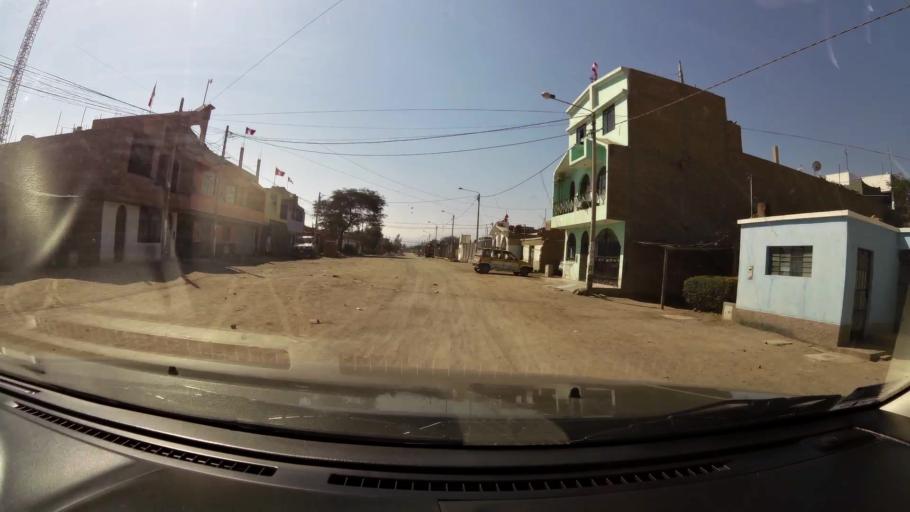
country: PE
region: Ica
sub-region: Provincia de Ica
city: La Tinguina
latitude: -14.0378
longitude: -75.7055
